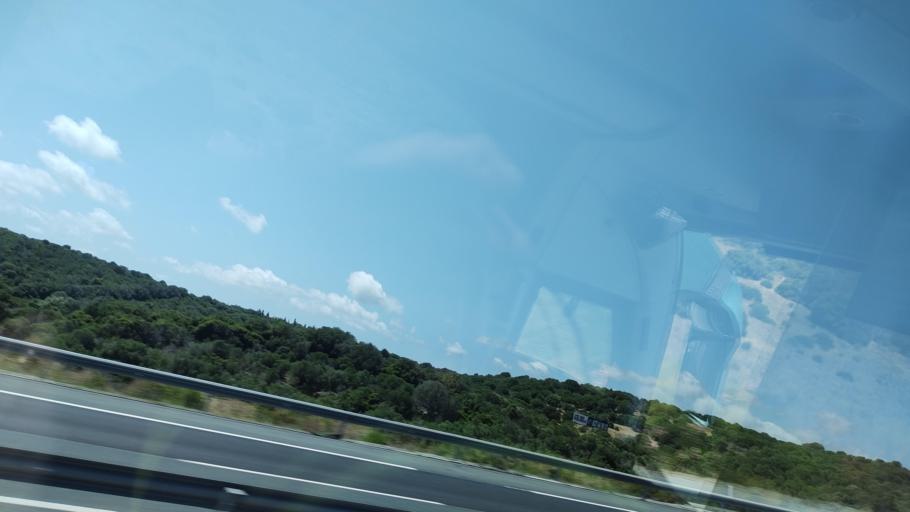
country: ES
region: Andalusia
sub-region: Provincia de Malaga
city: Manilva
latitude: 36.3142
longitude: -5.2749
